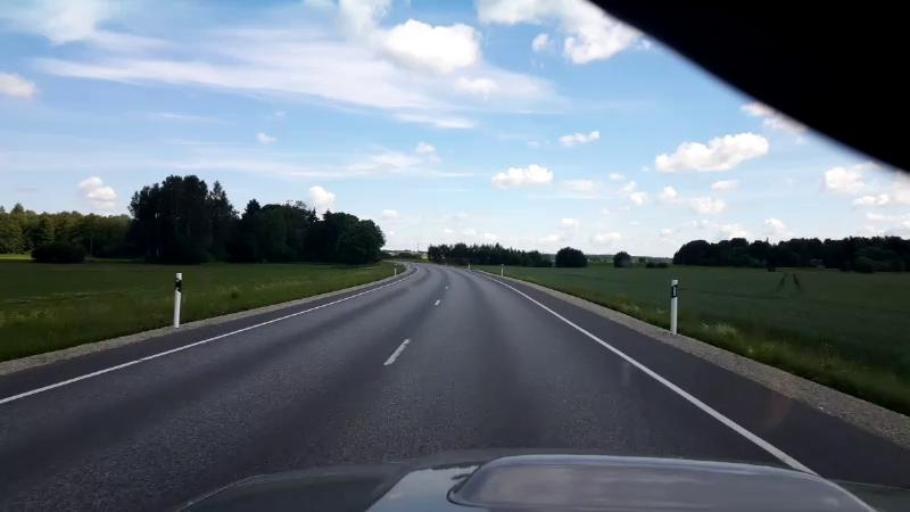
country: EE
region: Jaervamaa
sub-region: Jaerva-Jaani vald
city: Jarva-Jaani
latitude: 59.0144
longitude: 25.6993
